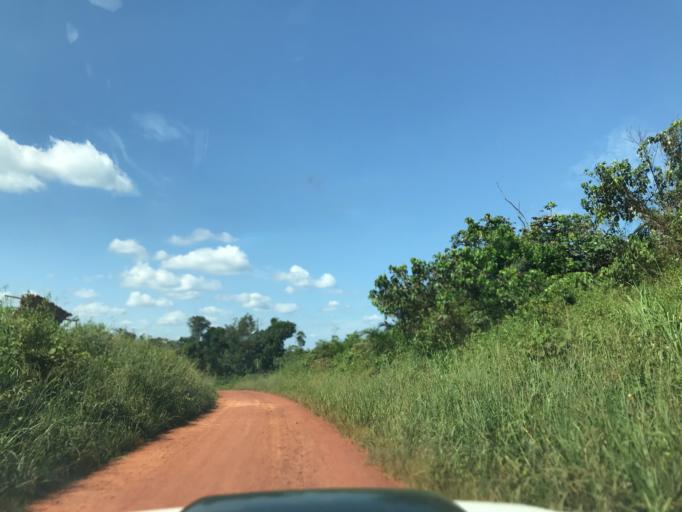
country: CD
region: Eastern Province
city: Kisangani
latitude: 1.2088
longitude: 25.2635
